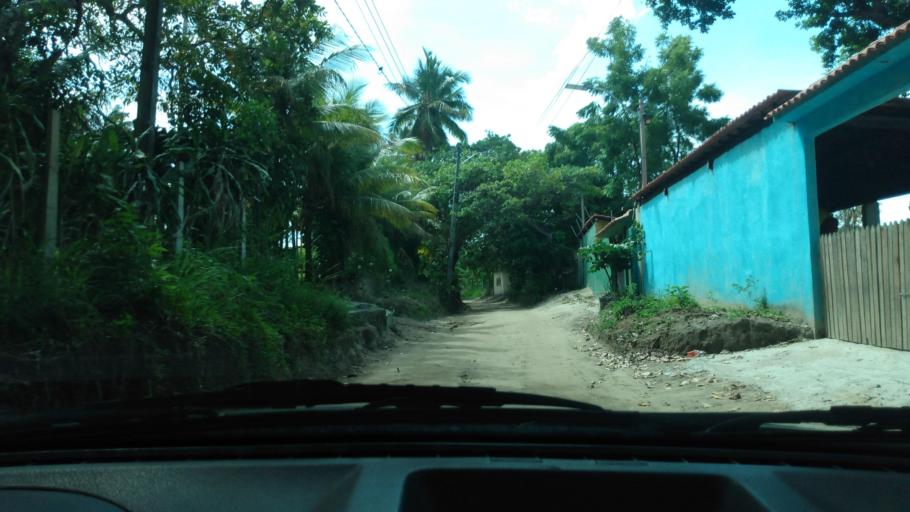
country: BR
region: Pernambuco
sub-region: Cabo De Santo Agostinho
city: Cabo
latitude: -8.3498
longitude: -34.9637
